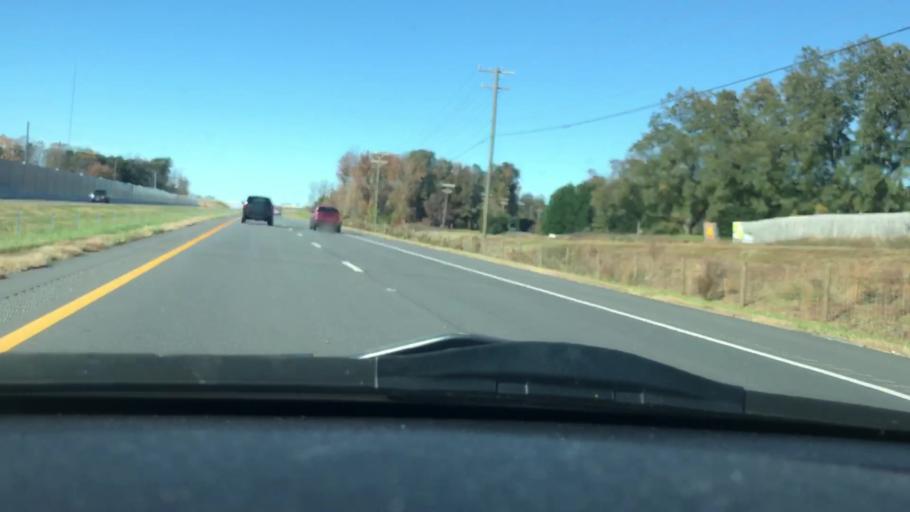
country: US
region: North Carolina
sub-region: Guilford County
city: Summerfield
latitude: 36.2590
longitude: -79.9256
